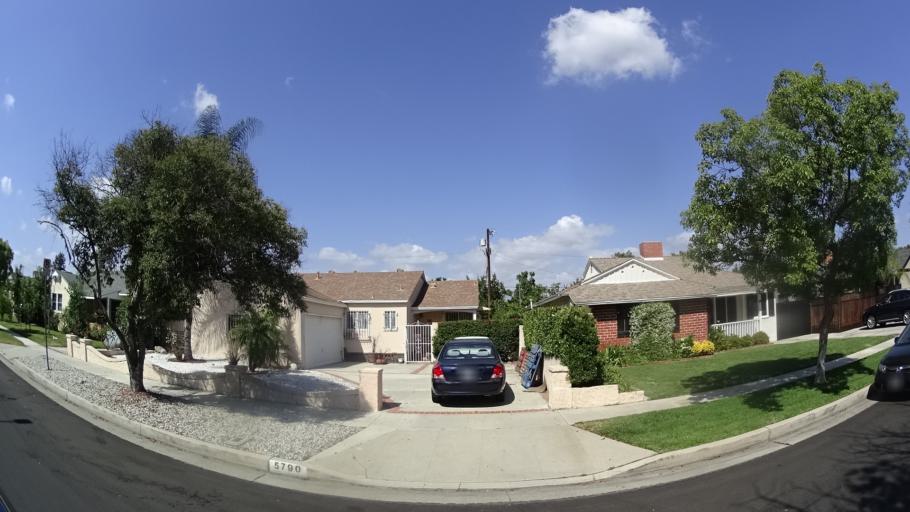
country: US
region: California
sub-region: Los Angeles County
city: North Hollywood
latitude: 34.1759
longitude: -118.3918
